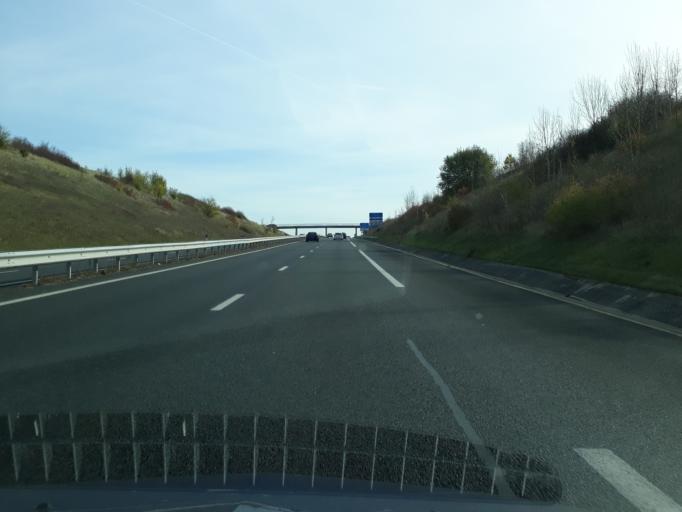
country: FR
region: Bourgogne
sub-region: Departement de l'Yonne
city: Thorigny-sur-Oreuse
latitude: 48.2474
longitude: 3.5402
